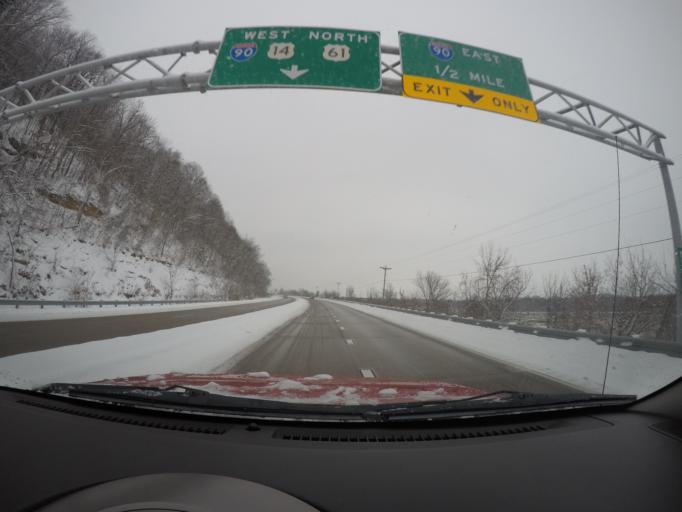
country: US
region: Minnesota
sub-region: Houston County
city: La Crescent
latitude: 43.8490
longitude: -91.2985
